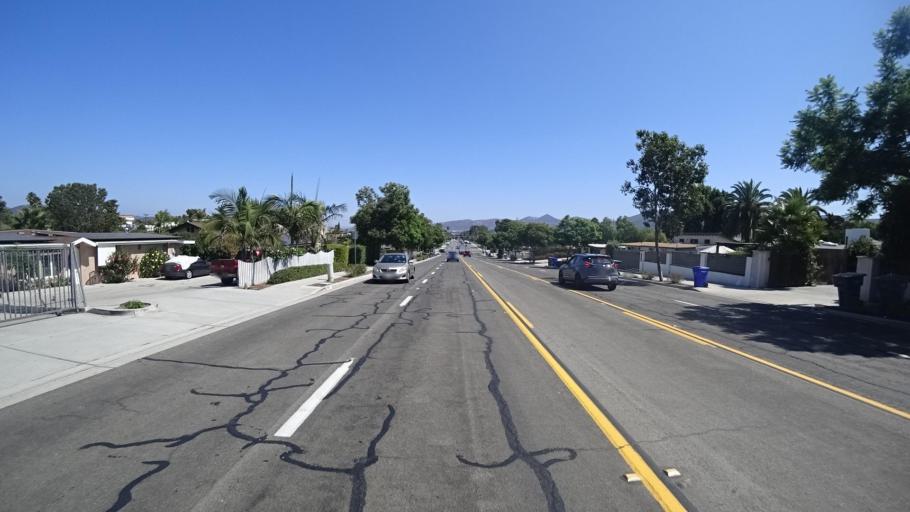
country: US
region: California
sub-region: San Diego County
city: Lake San Marcos
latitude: 33.1409
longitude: -117.2048
